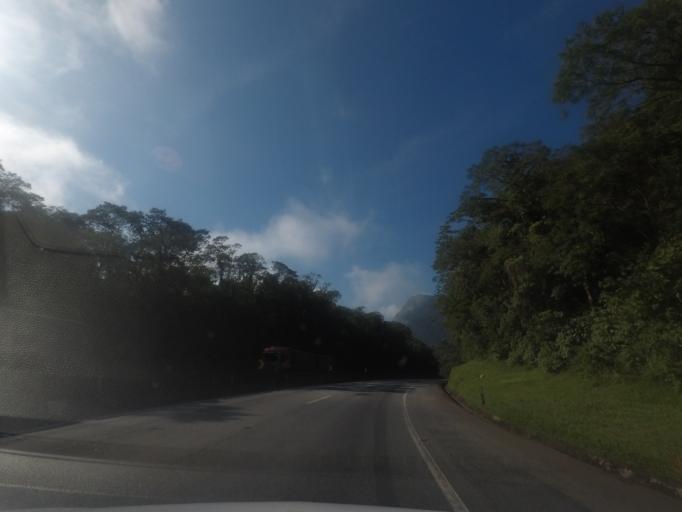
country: BR
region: Parana
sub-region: Piraquara
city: Piraquara
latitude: -25.5913
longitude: -48.8930
